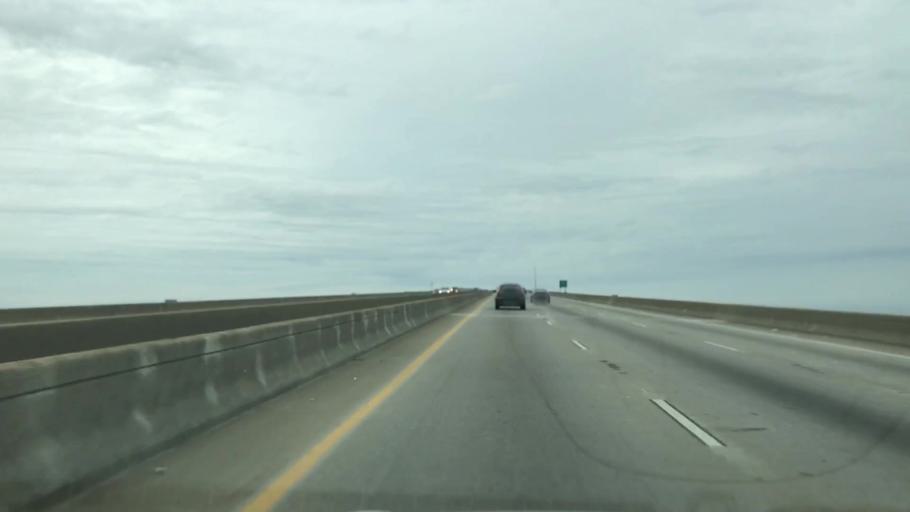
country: US
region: South Carolina
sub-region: Charleston County
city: Mount Pleasant
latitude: 32.8563
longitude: -79.8906
